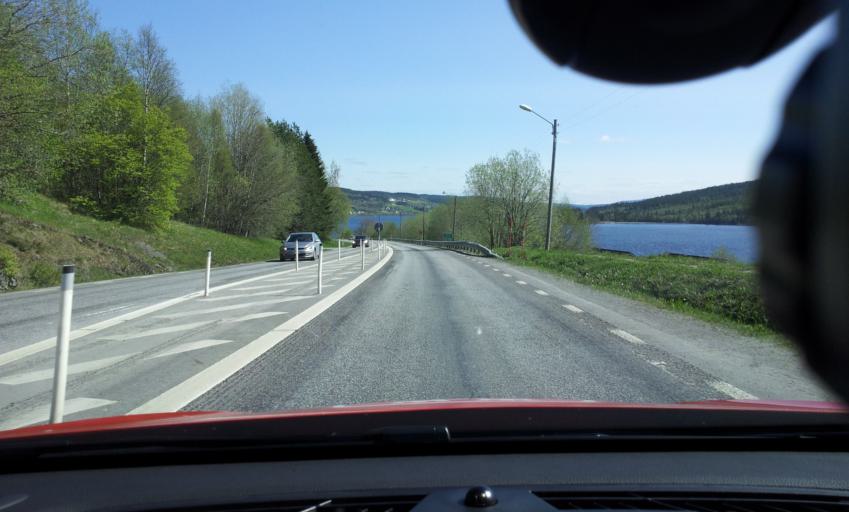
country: SE
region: Jaemtland
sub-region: Are Kommun
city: Are
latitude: 63.3895
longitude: 13.0997
